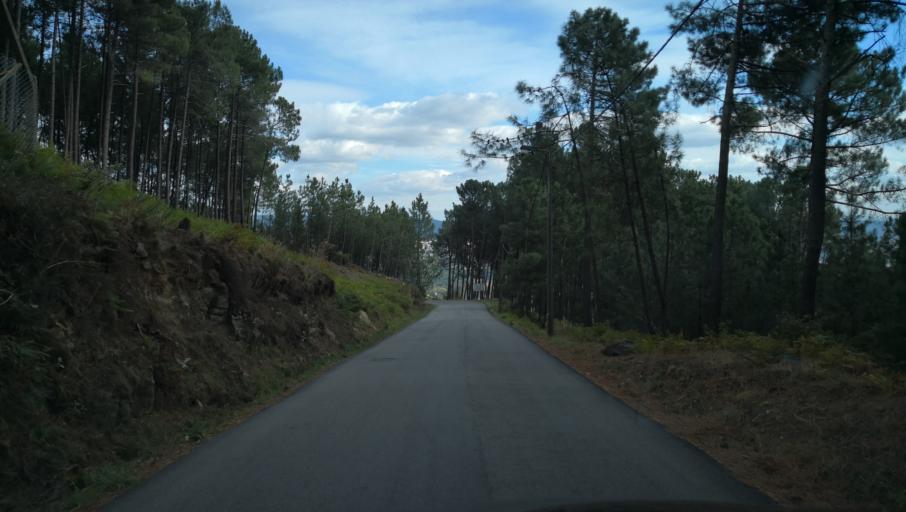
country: PT
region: Vila Real
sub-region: Vila Real
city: Vila Real
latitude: 41.3214
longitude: -7.7761
